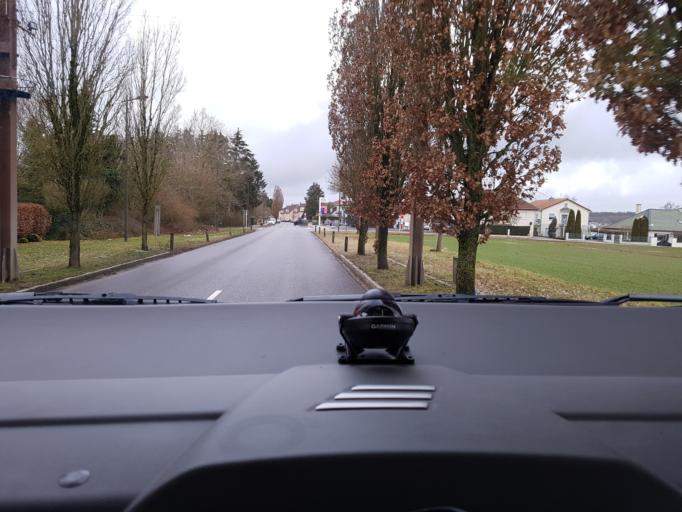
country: LU
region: Luxembourg
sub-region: Canton de Capellen
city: Steinfort
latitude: 49.6590
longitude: 5.9293
